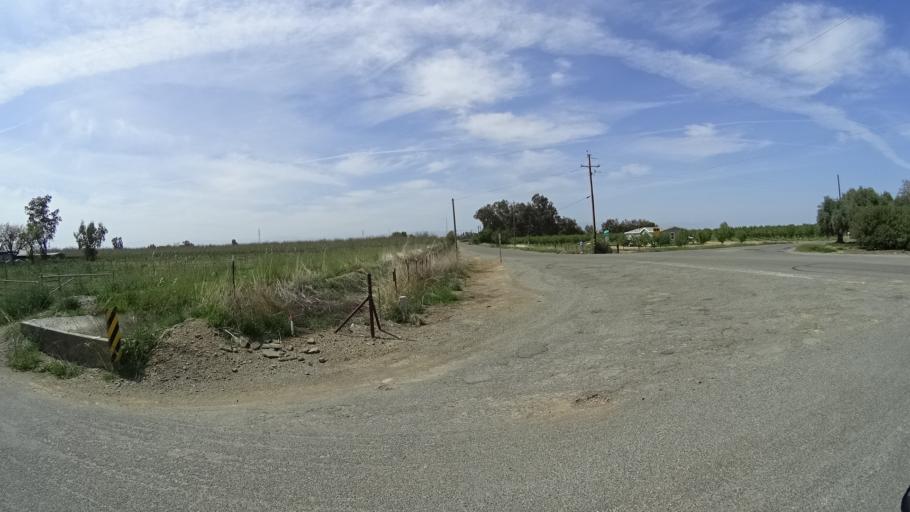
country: US
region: California
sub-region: Glenn County
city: Orland
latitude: 39.7975
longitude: -122.1592
